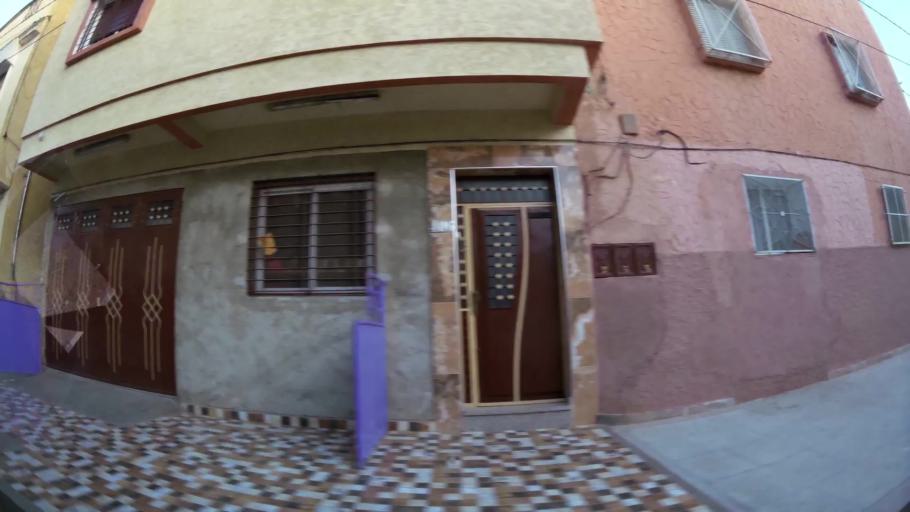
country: MA
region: Oriental
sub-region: Oujda-Angad
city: Oujda
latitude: 34.6807
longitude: -1.8857
